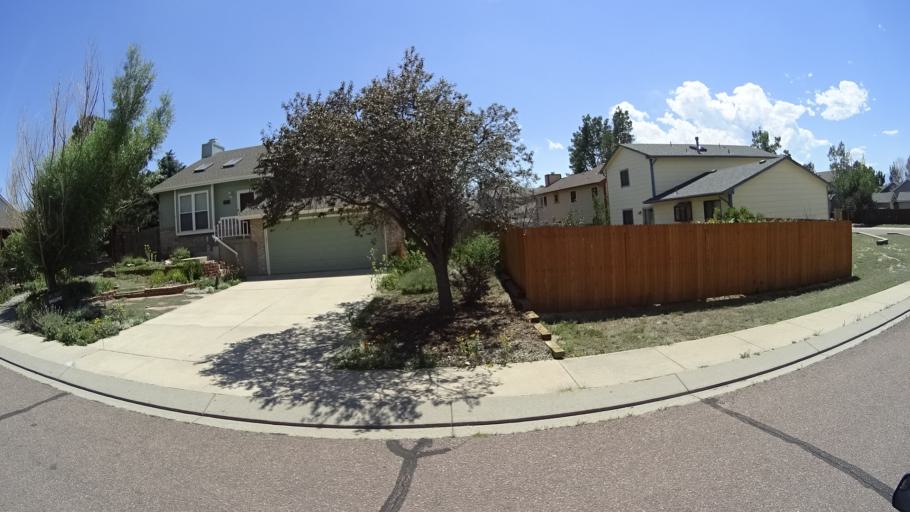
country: US
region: Colorado
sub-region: El Paso County
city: Black Forest
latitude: 38.9517
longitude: -104.7471
